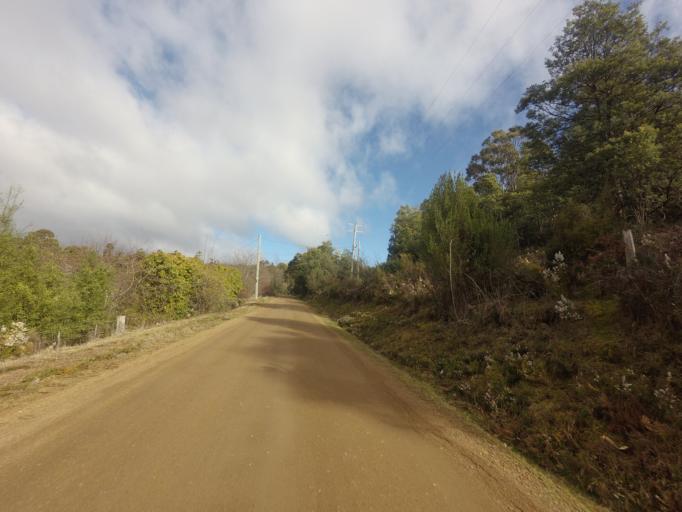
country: AU
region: Tasmania
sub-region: Derwent Valley
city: New Norfolk
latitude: -42.7902
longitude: 146.9309
